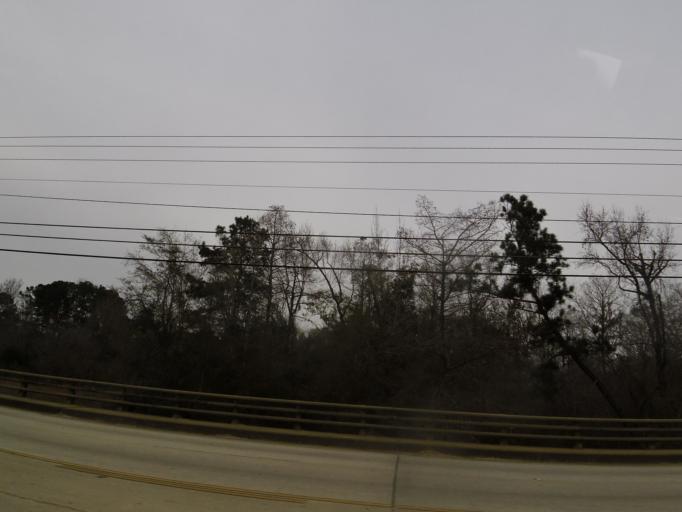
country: US
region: Georgia
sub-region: Grady County
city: Cairo
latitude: 30.8776
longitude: -84.1905
